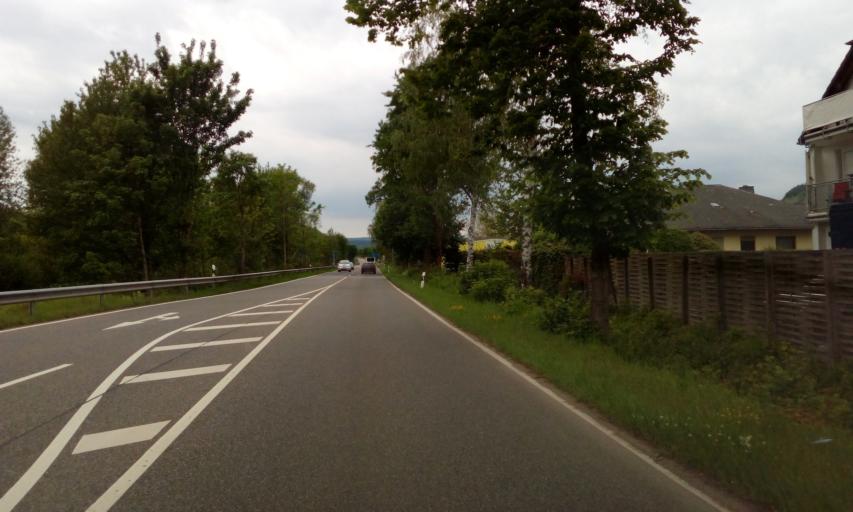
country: DE
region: Rheinland-Pfalz
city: Longuich
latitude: 49.8045
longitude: 6.7737
